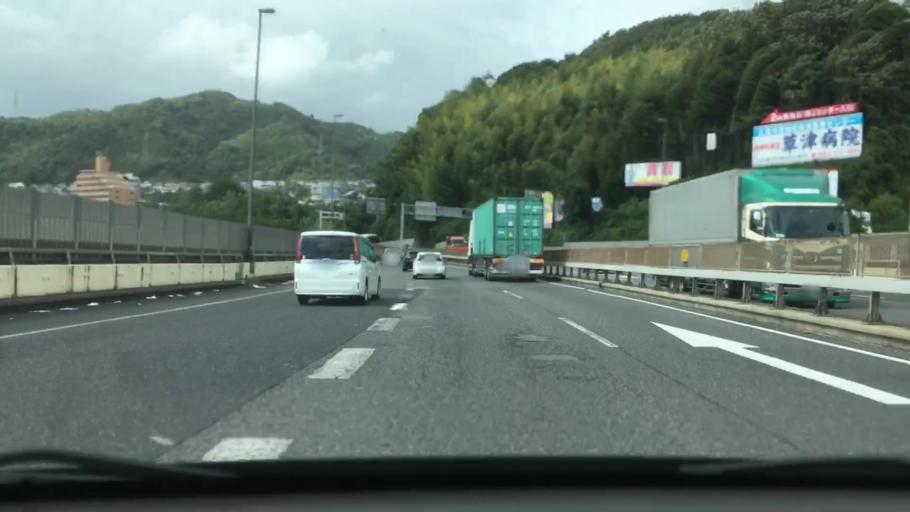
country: JP
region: Hiroshima
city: Hiroshima-shi
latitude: 34.3936
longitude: 132.4208
